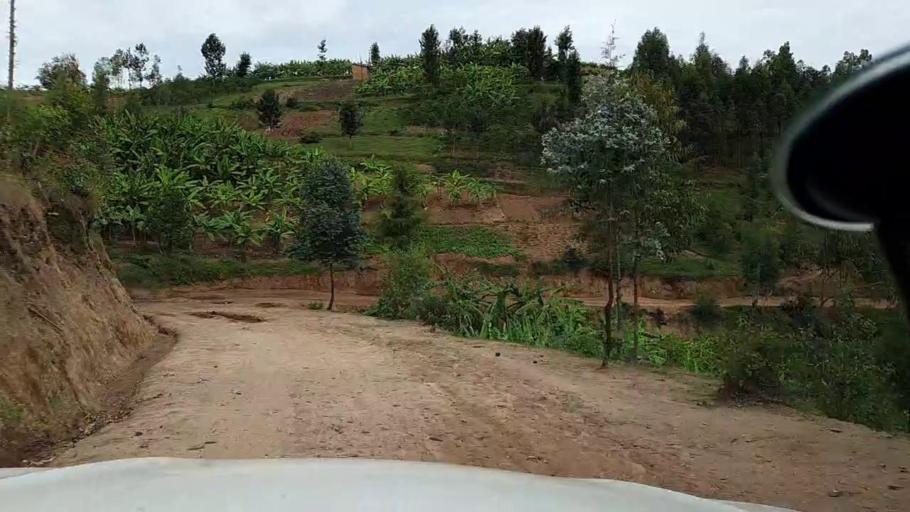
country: RW
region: Southern Province
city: Gitarama
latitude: -2.1295
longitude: 29.6611
